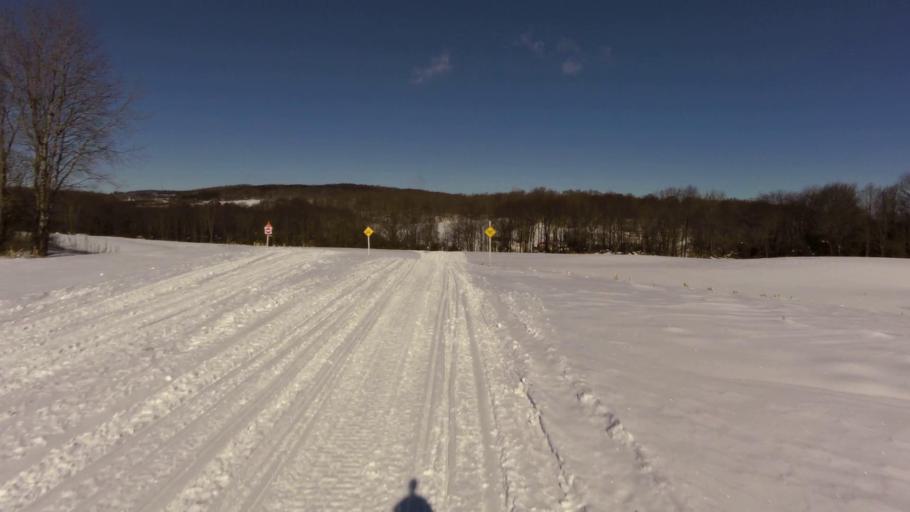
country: US
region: New York
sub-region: Cattaraugus County
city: Franklinville
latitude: 42.3904
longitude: -78.4836
